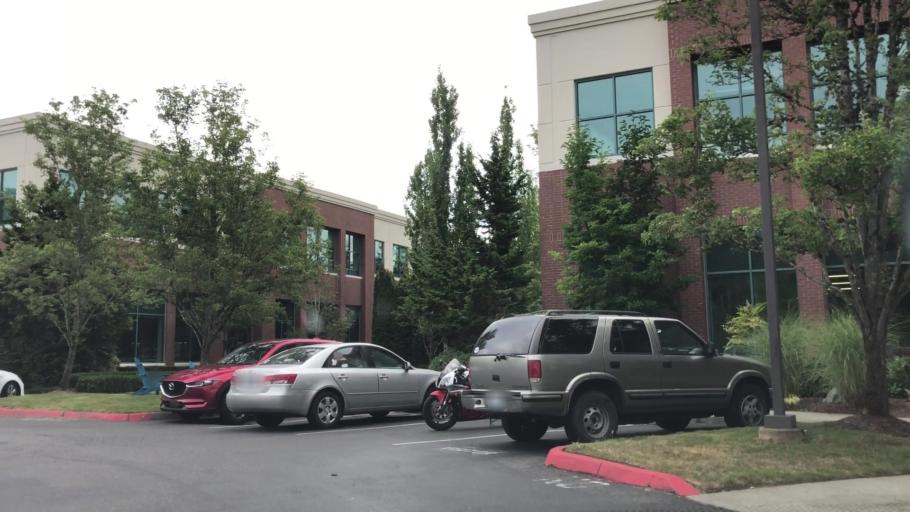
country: US
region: Washington
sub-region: King County
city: Bothell
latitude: 47.7724
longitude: -122.1854
